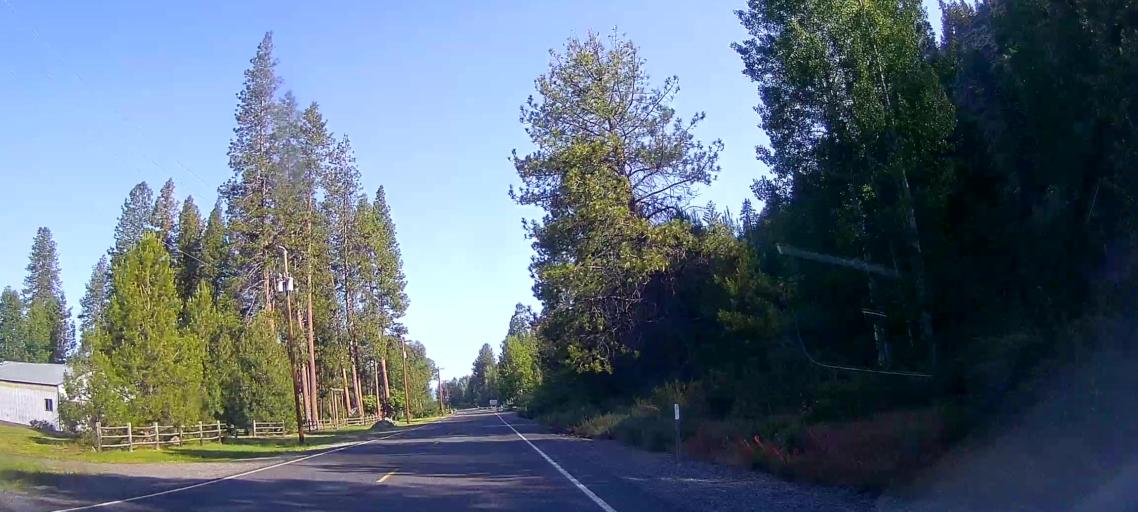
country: US
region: Oregon
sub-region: Klamath County
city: Klamath Falls
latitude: 42.6401
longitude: -121.9420
